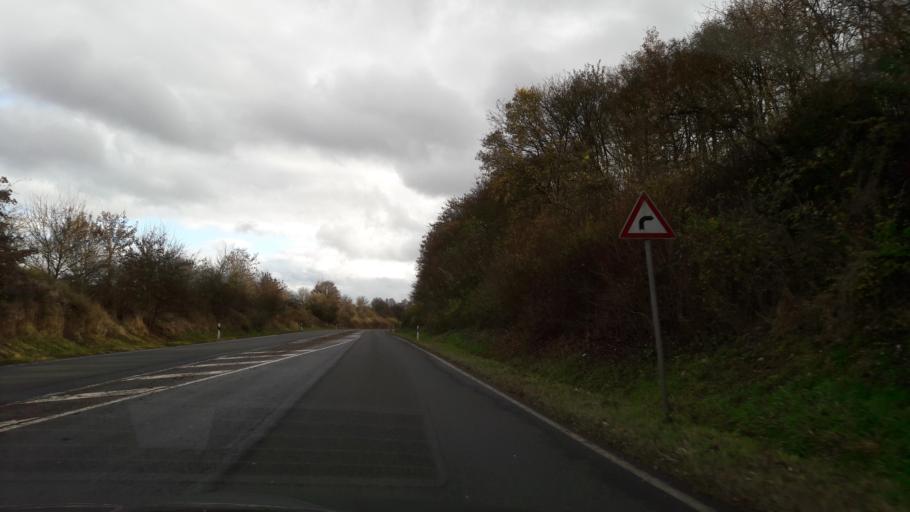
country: DE
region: Rheinland-Pfalz
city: Fell
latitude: 49.7635
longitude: 6.7622
